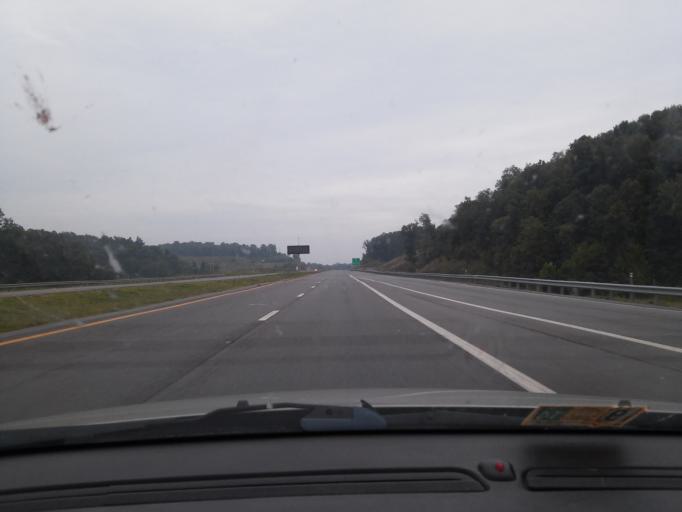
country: US
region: West Virginia
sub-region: Putnam County
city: Teays Valley
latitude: 38.4788
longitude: -81.9229
